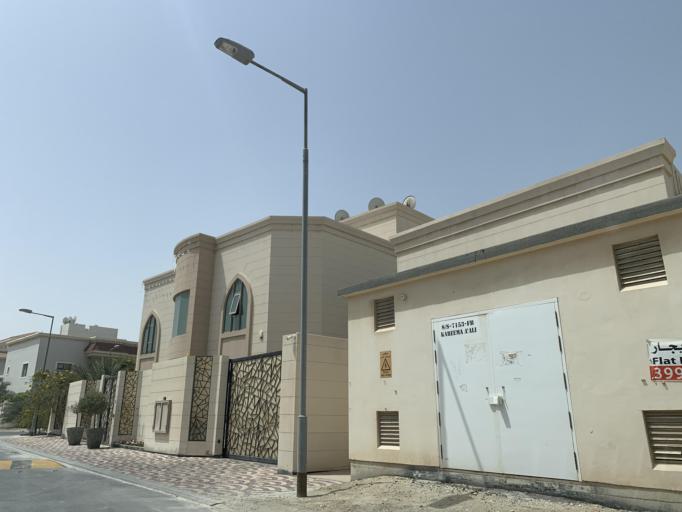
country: BH
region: Northern
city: Madinat `Isa
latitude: 26.1648
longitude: 50.5221
